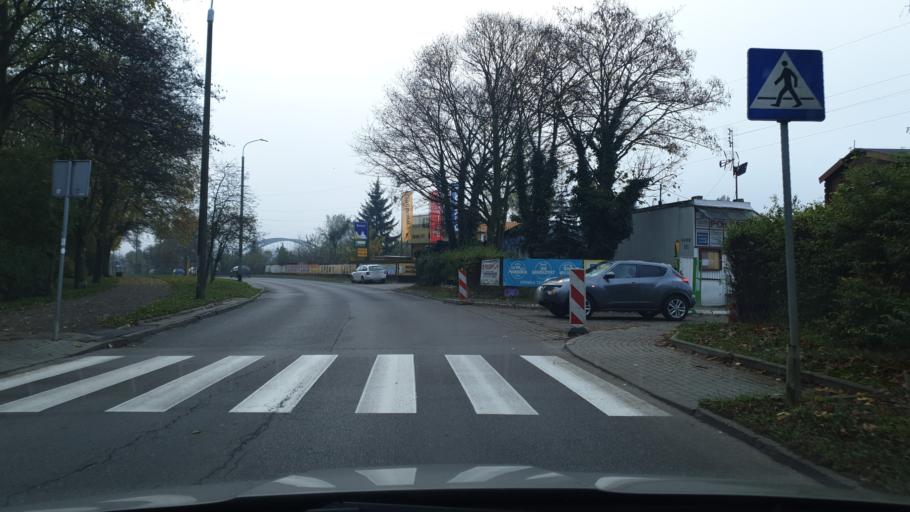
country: PL
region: Pomeranian Voivodeship
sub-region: Sopot
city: Sopot
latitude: 54.3954
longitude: 18.5867
